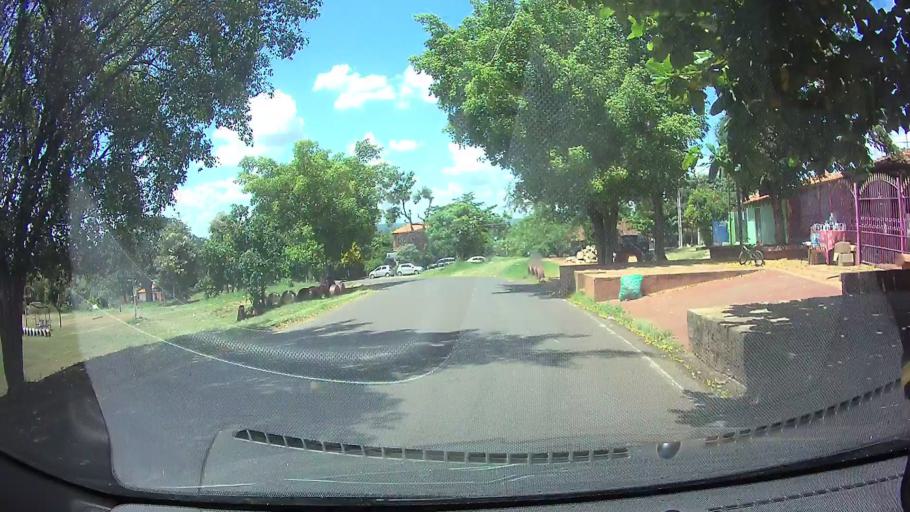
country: PY
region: Central
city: Limpio
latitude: -25.1519
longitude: -57.4523
